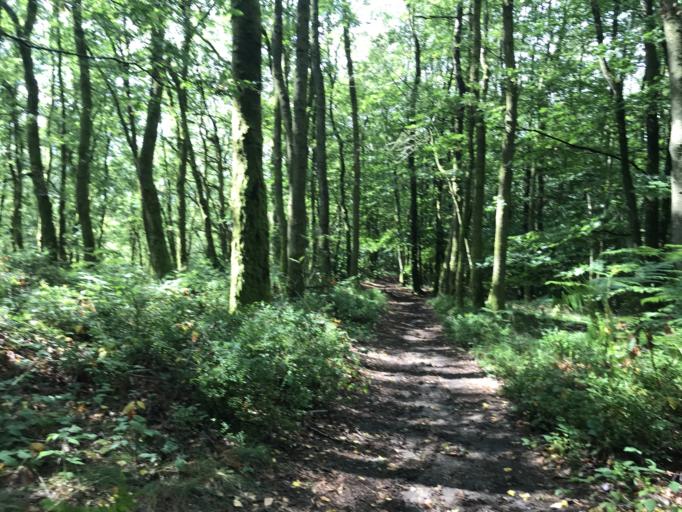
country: FR
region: Champagne-Ardenne
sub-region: Departement des Ardennes
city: Thilay
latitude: 49.8834
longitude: 4.7837
